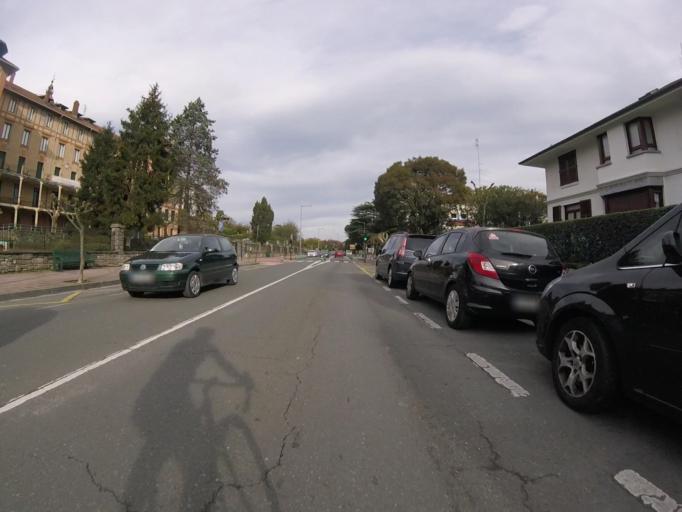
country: ES
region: Basque Country
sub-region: Provincia de Guipuzcoa
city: Fuenterrabia
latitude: 43.3621
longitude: -1.7899
